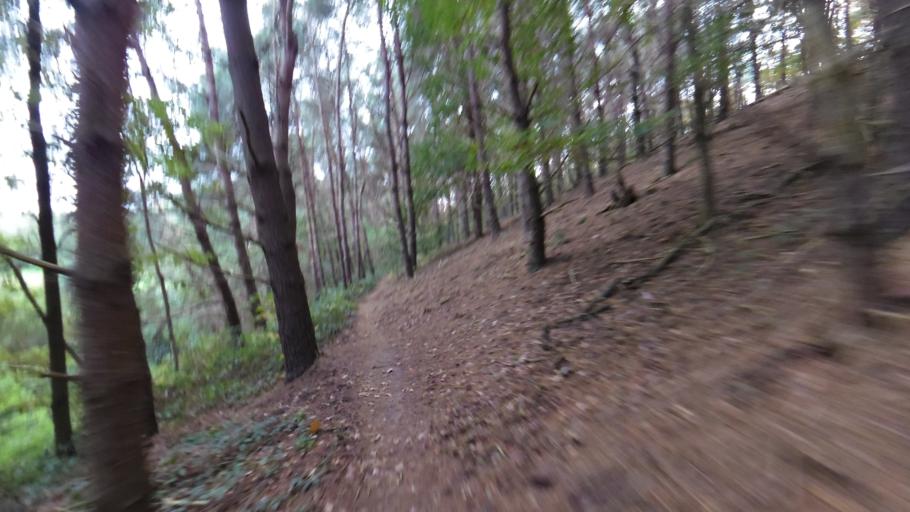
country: NL
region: Gelderland
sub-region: Gemeente Ede
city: Lunteren
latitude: 52.0989
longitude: 5.6548
